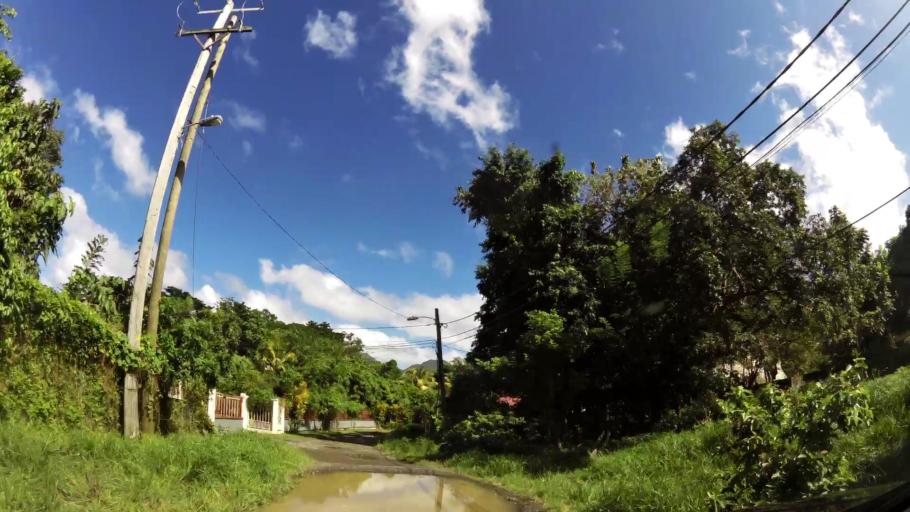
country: DM
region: Saint John
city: Portsmouth
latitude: 15.5599
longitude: -61.4584
